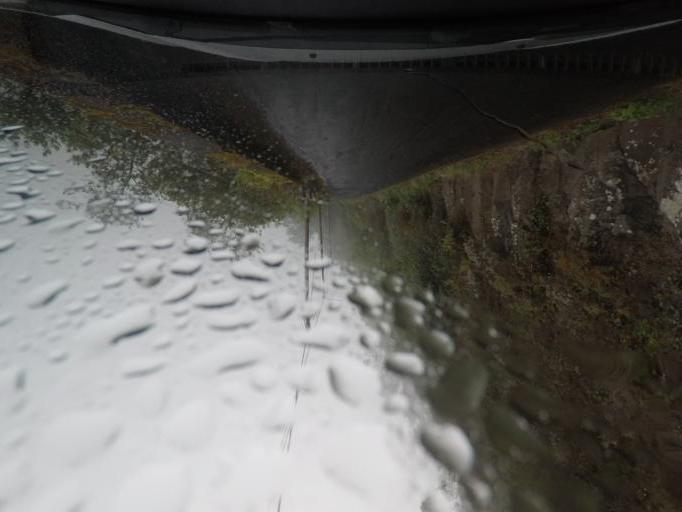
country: PT
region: Madeira
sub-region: Santana
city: Santana
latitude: 32.7564
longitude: -16.8712
